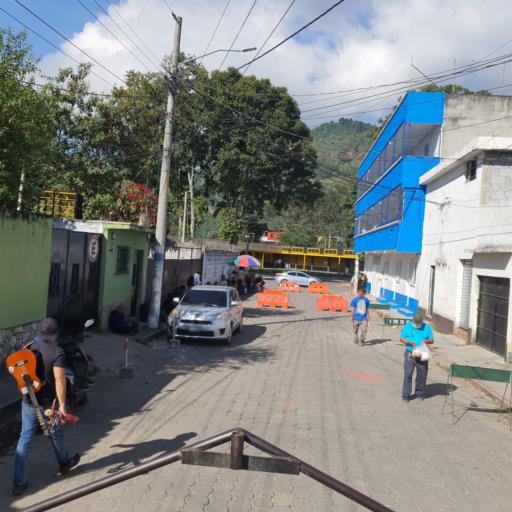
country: GT
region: Guatemala
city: Villa Canales
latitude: 14.4779
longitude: -90.5344
